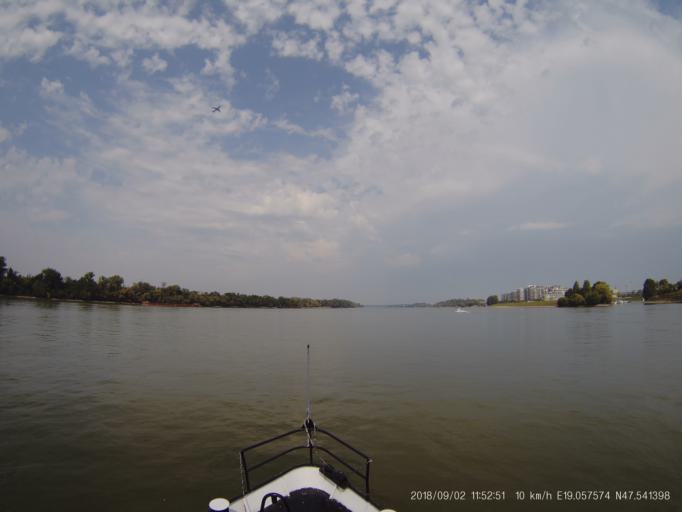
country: HU
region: Budapest
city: Budapest III. keruelet
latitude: 47.5406
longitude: 19.0576
